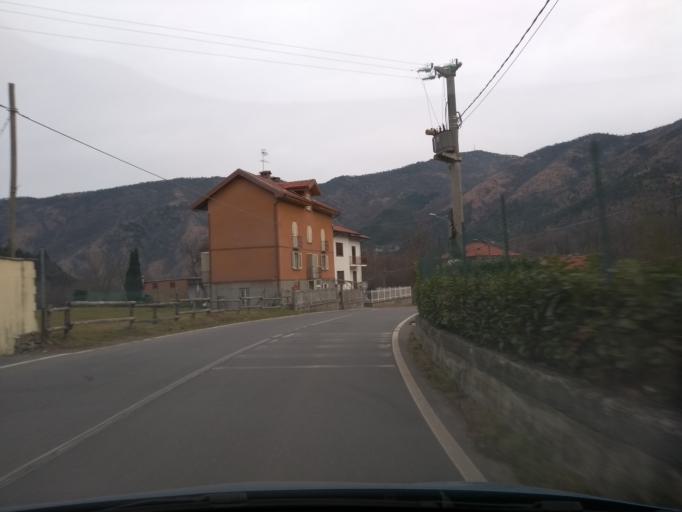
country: IT
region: Piedmont
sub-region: Provincia di Torino
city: Germagnano
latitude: 45.2655
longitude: 7.4527
